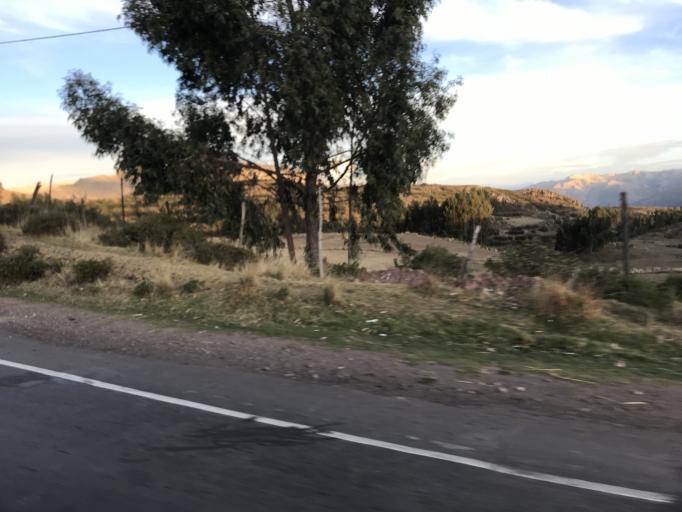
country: PE
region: Cusco
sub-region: Provincia de Cusco
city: Cusco
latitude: -13.4926
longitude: -71.9671
